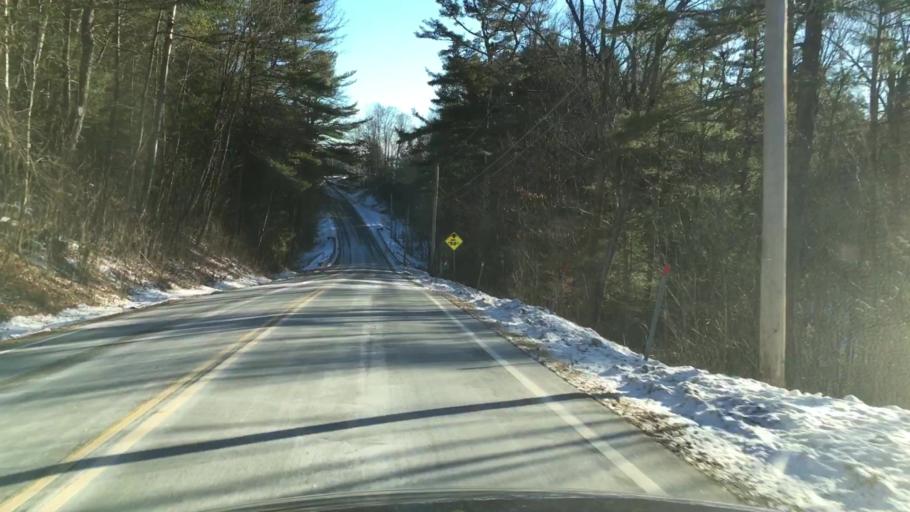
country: US
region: New Hampshire
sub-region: Grafton County
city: Woodsville
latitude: 44.1942
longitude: -72.0561
